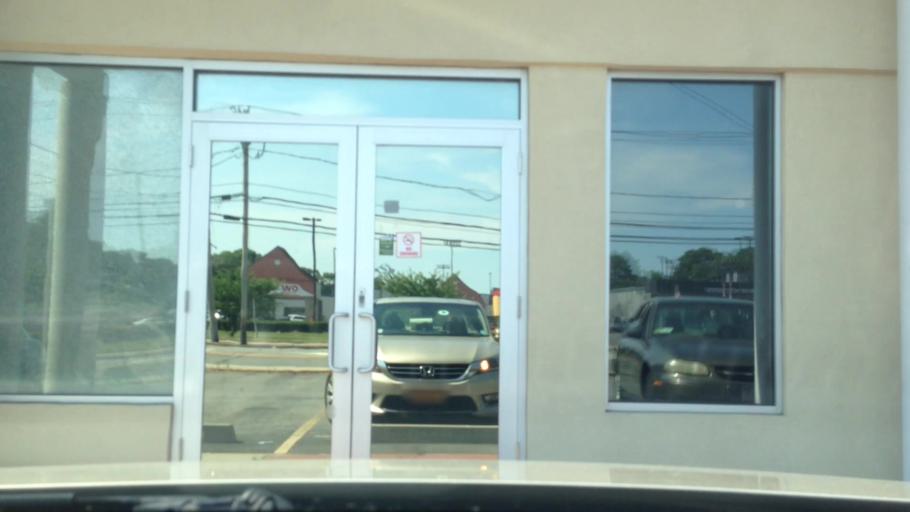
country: US
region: New York
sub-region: Suffolk County
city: Centereach
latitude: 40.8602
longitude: -73.0747
